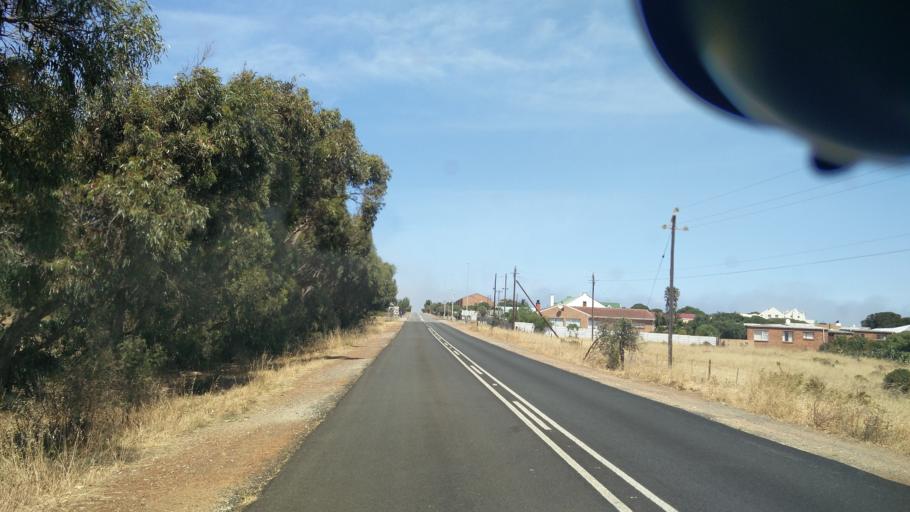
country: ZA
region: Western Cape
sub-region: City of Cape Town
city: Atlantis
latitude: -33.3434
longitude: 18.1692
